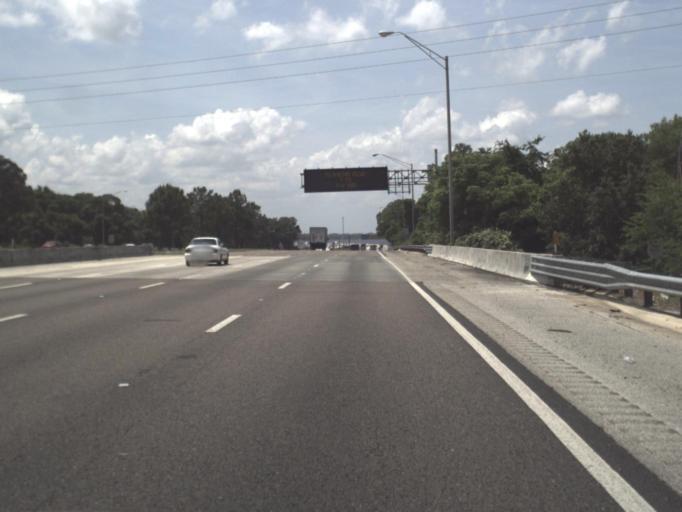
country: US
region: Florida
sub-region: Saint Johns County
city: Fruit Cove
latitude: 30.1840
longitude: -81.6345
